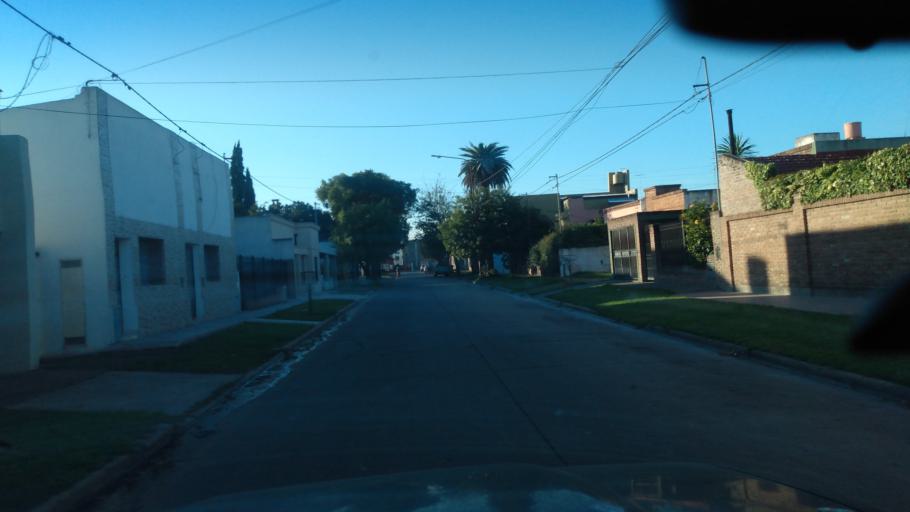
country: AR
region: Buenos Aires
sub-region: Partido de Lujan
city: Lujan
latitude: -34.5667
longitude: -59.0976
